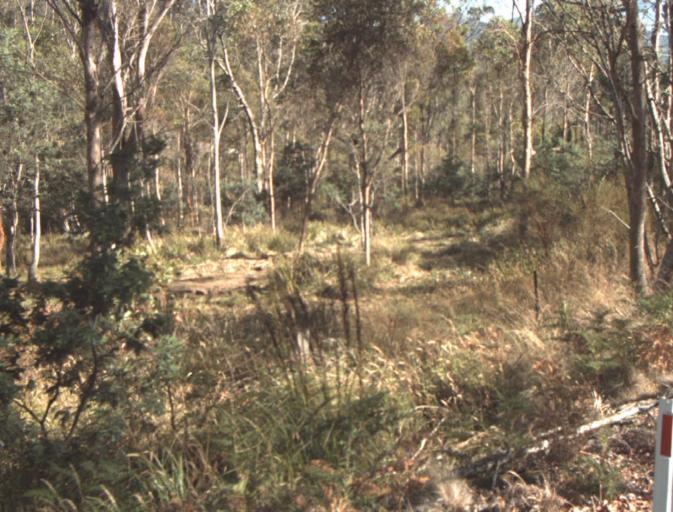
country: AU
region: Tasmania
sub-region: Launceston
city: Newstead
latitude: -41.3692
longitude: 147.3001
